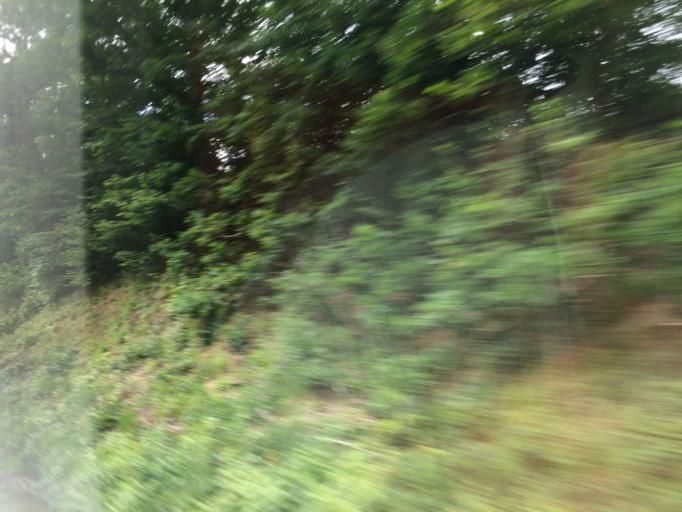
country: DK
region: South Denmark
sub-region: Vejle Kommune
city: Borkop
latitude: 55.6911
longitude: 9.6059
